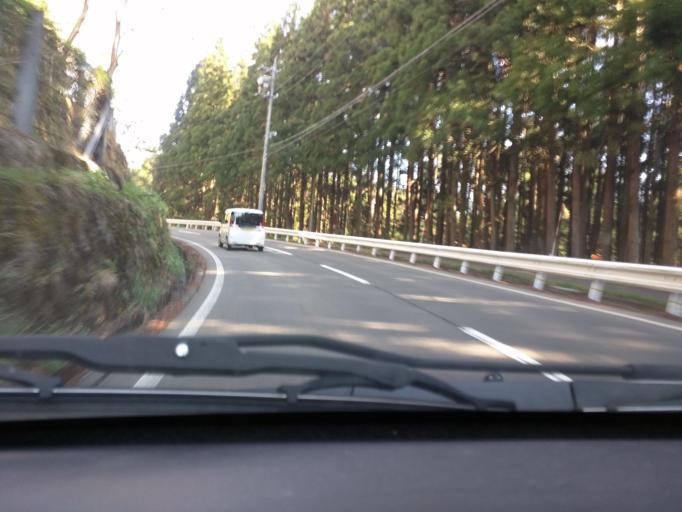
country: JP
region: Nagano
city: Nagano-shi
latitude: 36.6967
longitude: 138.1546
